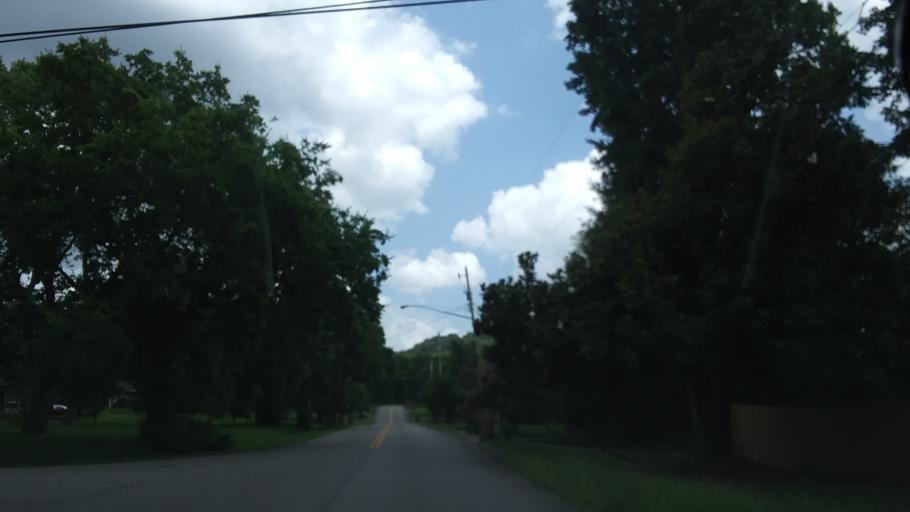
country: US
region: Tennessee
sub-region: Davidson County
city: Belle Meade
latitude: 36.1358
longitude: -86.8820
